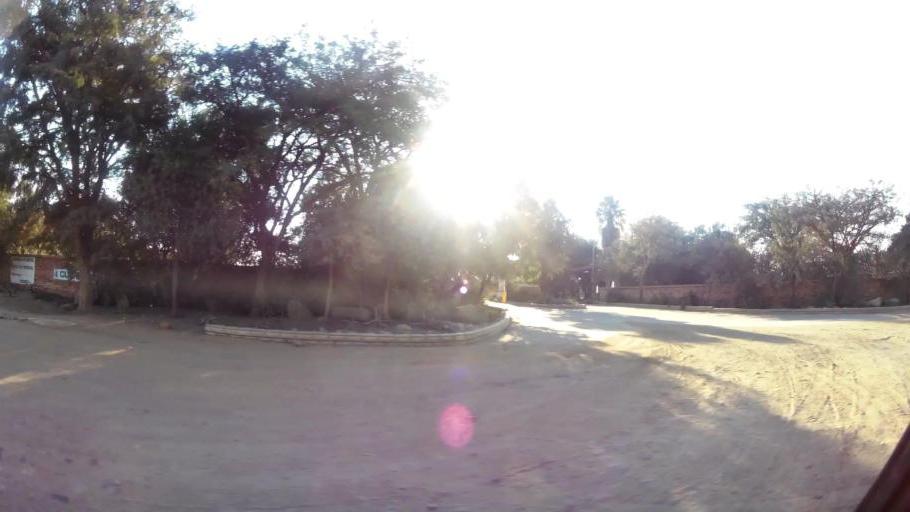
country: ZA
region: Gauteng
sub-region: City of Johannesburg Metropolitan Municipality
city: Diepsloot
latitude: -25.9811
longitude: 27.9419
